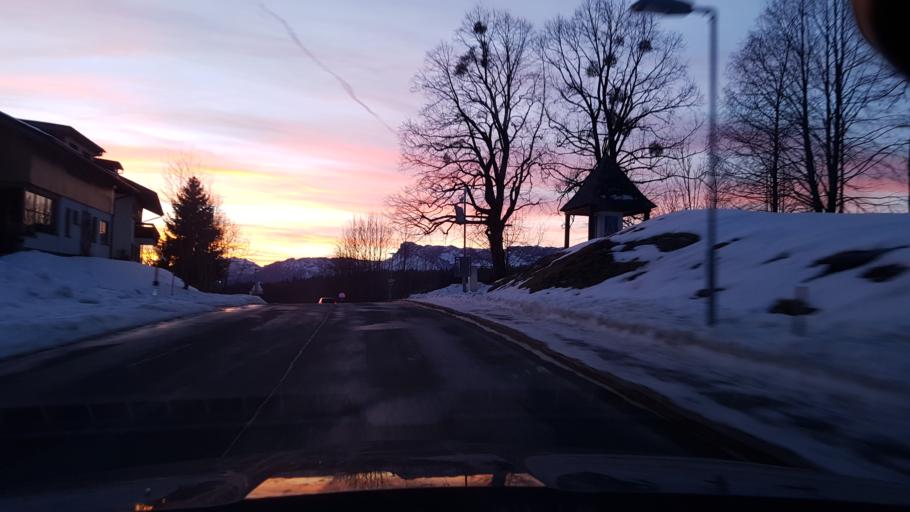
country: AT
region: Salzburg
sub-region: Politischer Bezirk Hallein
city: Krispl
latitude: 47.7157
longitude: 13.1788
